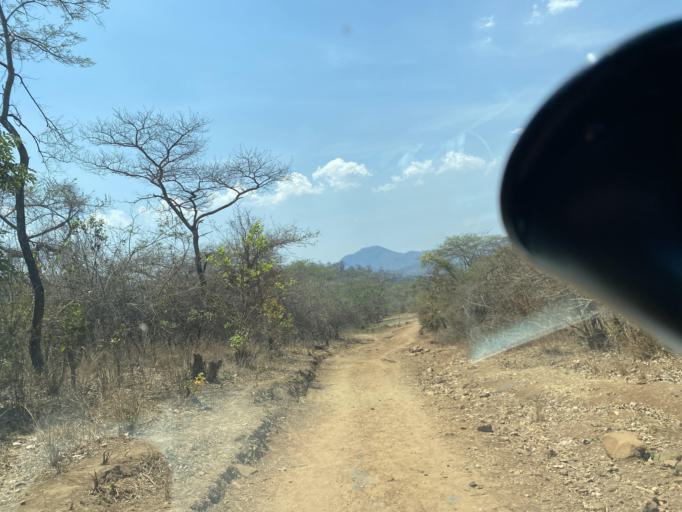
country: ZM
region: Lusaka
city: Kafue
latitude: -15.7913
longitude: 28.4559
